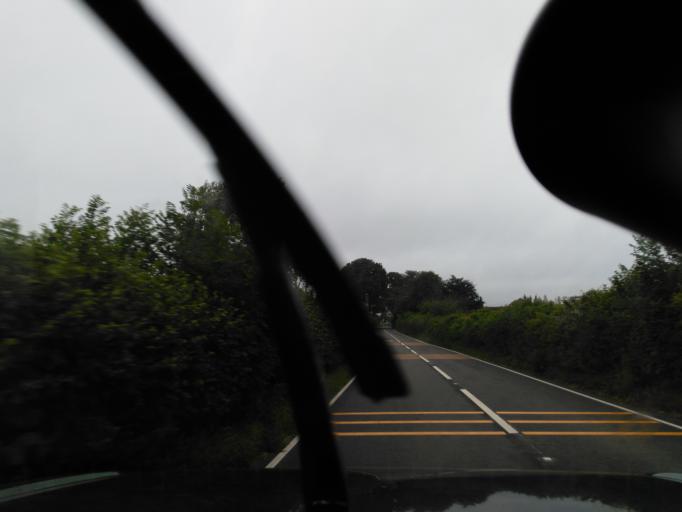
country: GB
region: England
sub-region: Dorset
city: Shaftesbury
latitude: 50.9416
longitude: -2.1934
